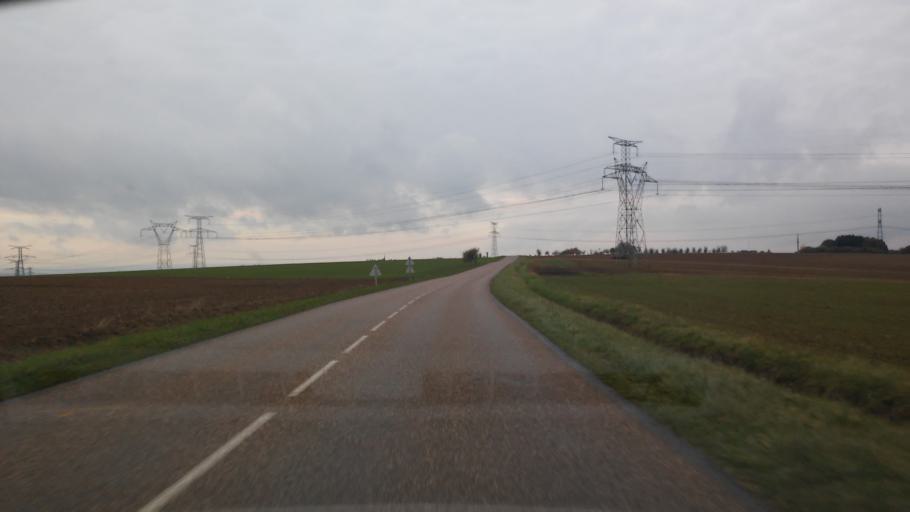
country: FR
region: Lorraine
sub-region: Departement de la Moselle
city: Vigy
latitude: 49.1862
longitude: 6.3074
